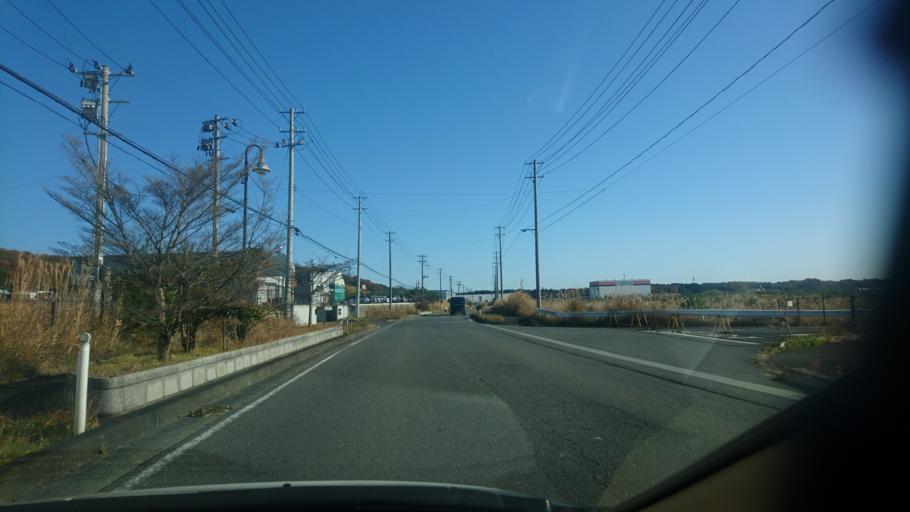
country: JP
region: Miyagi
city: Tomiya
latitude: 38.4624
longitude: 140.9327
